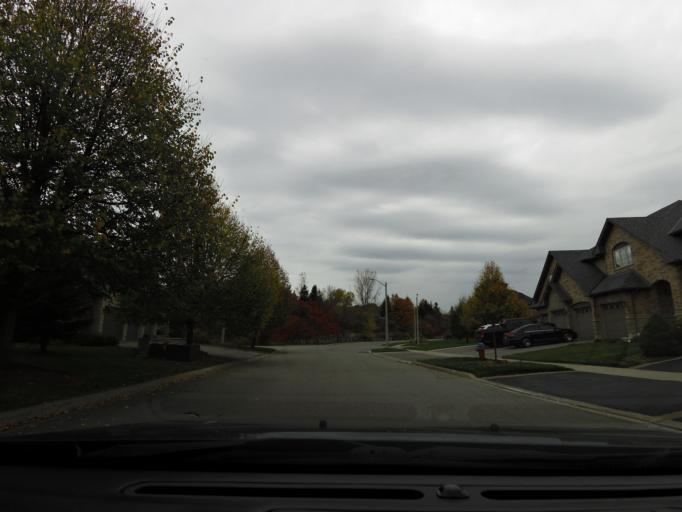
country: CA
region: Ontario
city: Hamilton
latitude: 43.2993
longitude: -79.8740
